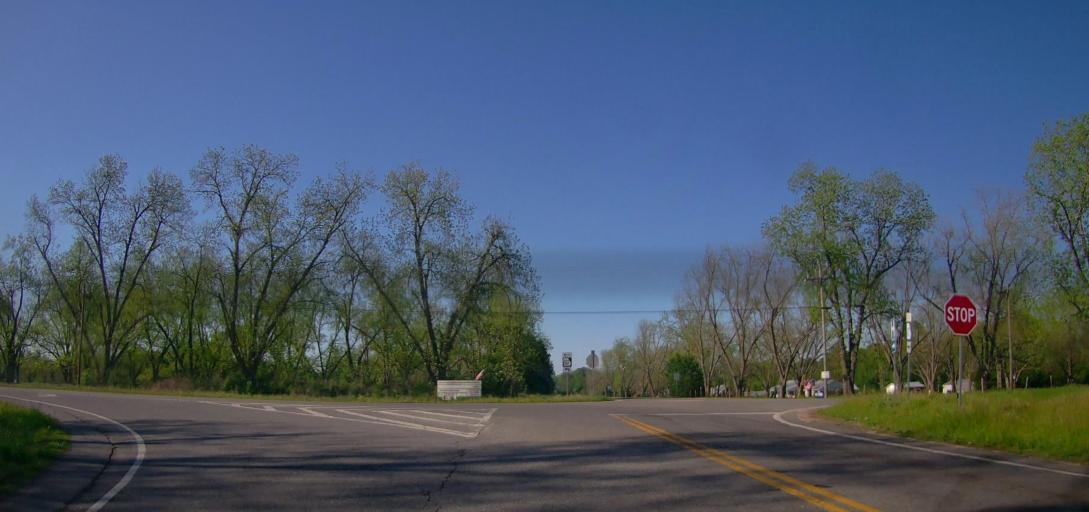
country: US
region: Georgia
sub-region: Ben Hill County
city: Fitzgerald
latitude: 31.7177
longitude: -83.3101
